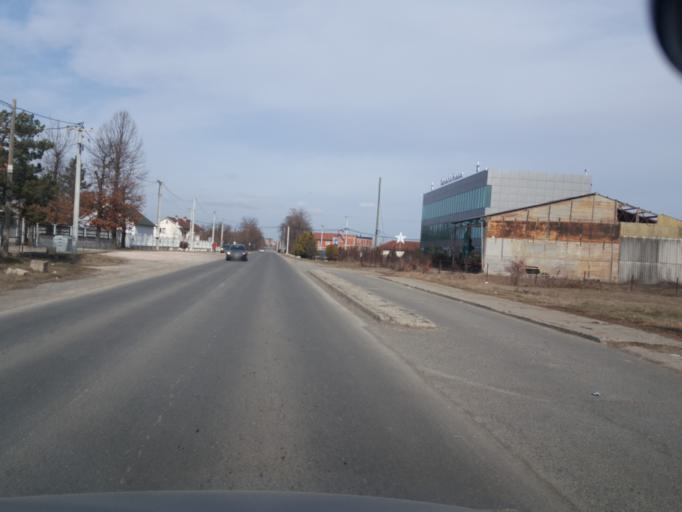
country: XK
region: Gjakova
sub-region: Komuna e Gjakoves
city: Gjakove
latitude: 42.4185
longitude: 20.4356
